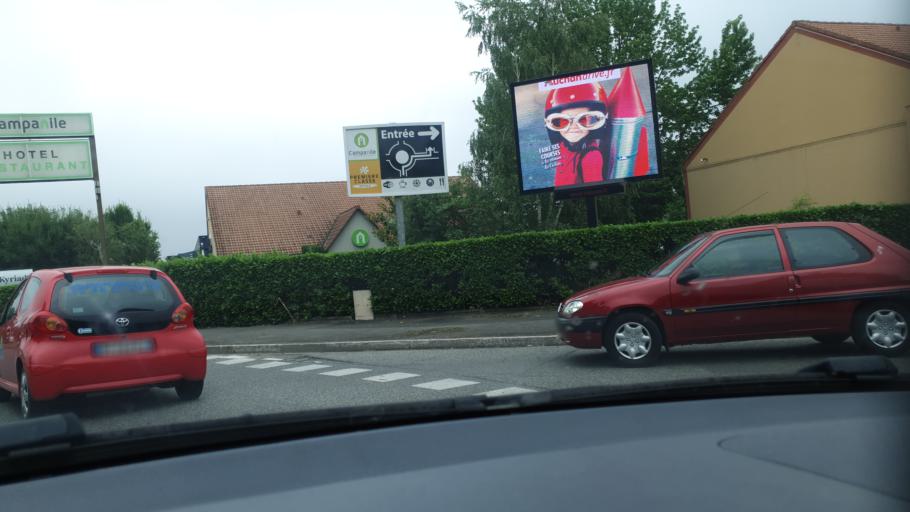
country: FR
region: Midi-Pyrenees
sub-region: Departement des Hautes-Pyrenees
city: Juillan
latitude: 43.2221
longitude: 0.0428
